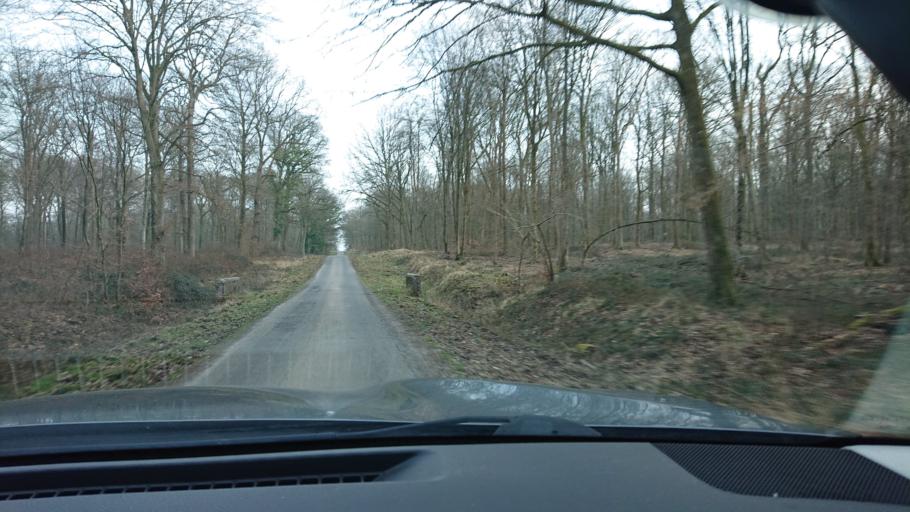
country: FR
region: Nord-Pas-de-Calais
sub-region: Departement du Nord
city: Landrecies
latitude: 50.1621
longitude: 3.7107
